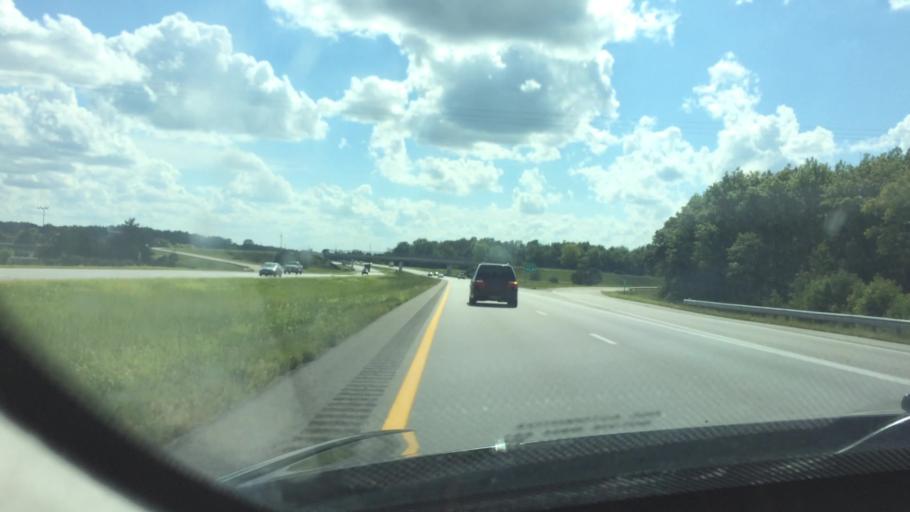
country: US
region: Ohio
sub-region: Shelby County
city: Sidney
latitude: 40.3164
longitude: -84.1720
